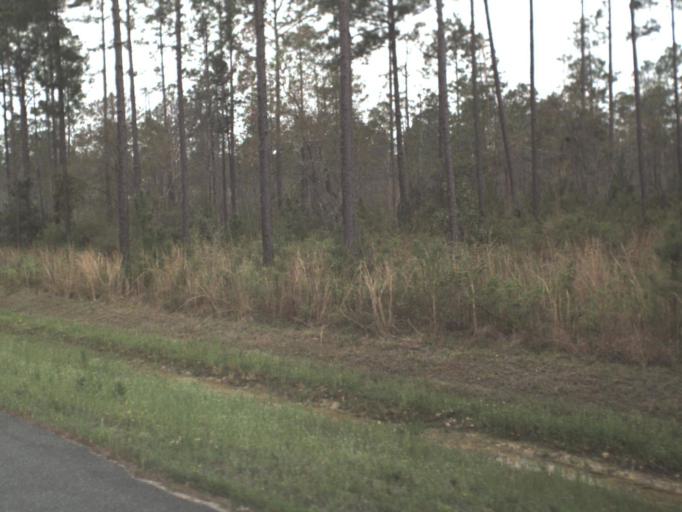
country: US
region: Florida
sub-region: Calhoun County
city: Blountstown
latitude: 30.4328
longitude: -85.1894
